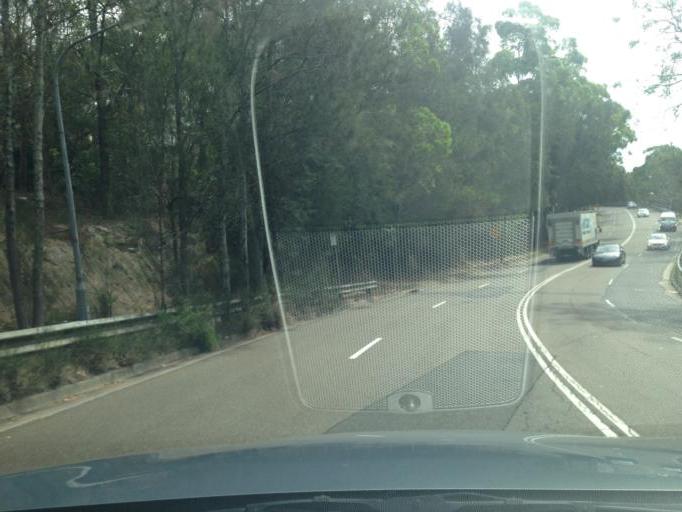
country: AU
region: New South Wales
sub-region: Lane Cove
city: Lane Cove West
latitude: -33.8072
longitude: 151.1525
